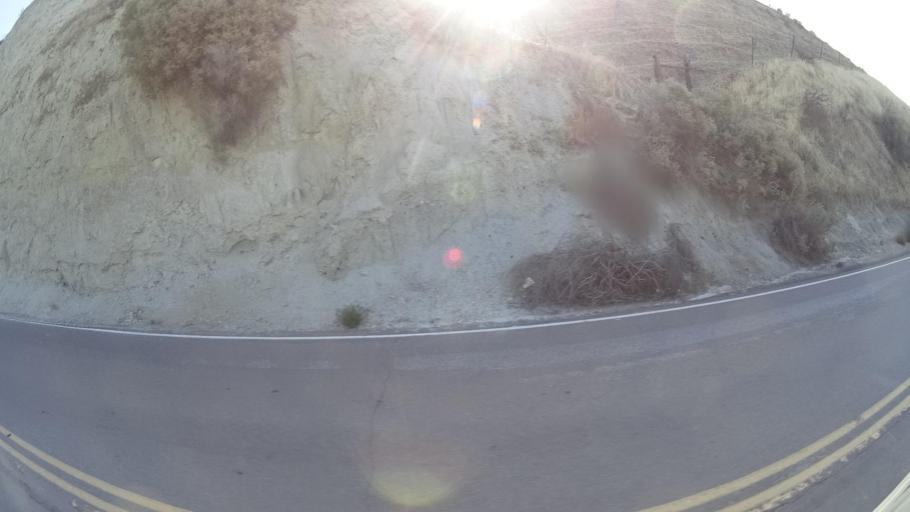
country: US
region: California
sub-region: Kern County
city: Oildale
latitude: 35.5345
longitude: -118.9602
